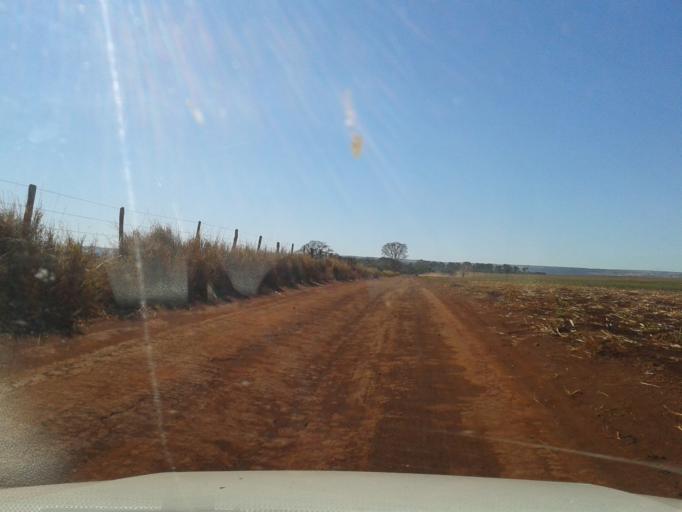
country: BR
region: Minas Gerais
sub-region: Centralina
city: Centralina
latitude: -18.5904
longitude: -49.1622
